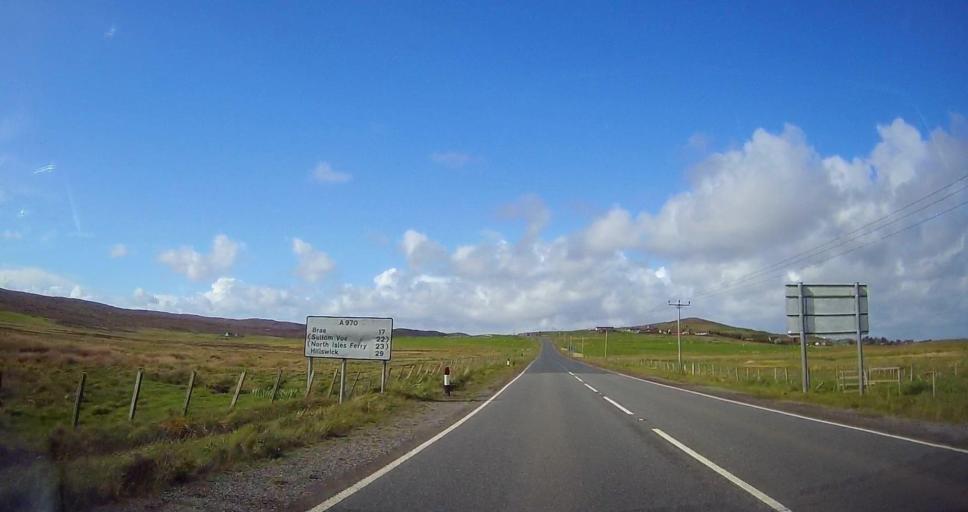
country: GB
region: Scotland
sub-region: Shetland Islands
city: Lerwick
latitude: 60.1919
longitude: -1.2322
